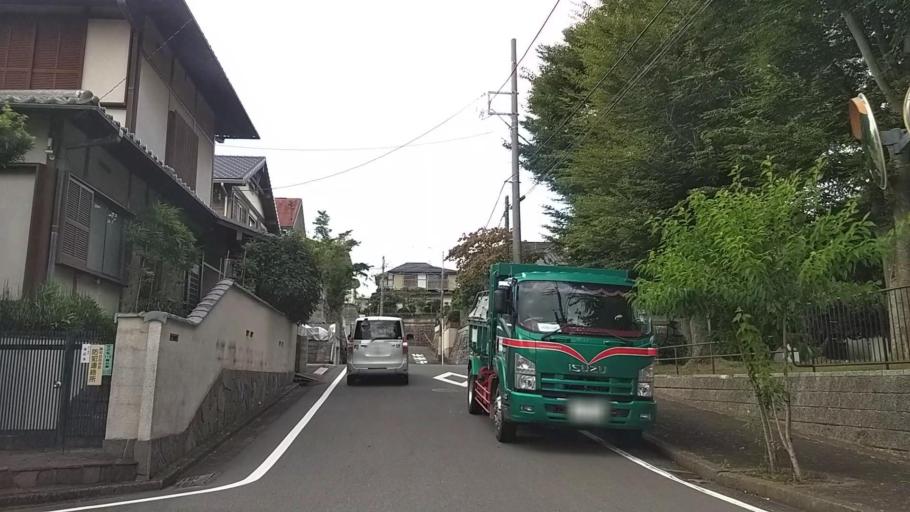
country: JP
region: Kanagawa
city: Yokohama
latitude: 35.4804
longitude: 139.5625
